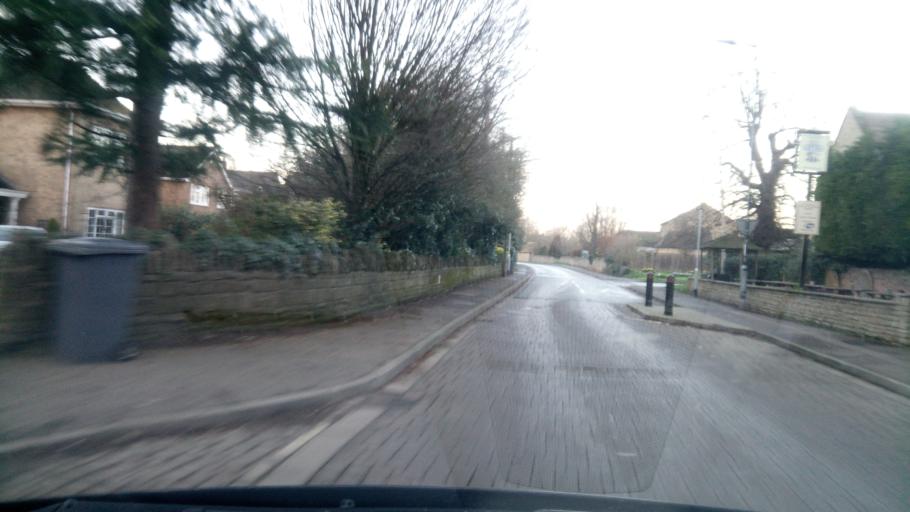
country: GB
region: England
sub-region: Peterborough
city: Castor
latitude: 52.5731
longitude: -0.3466
